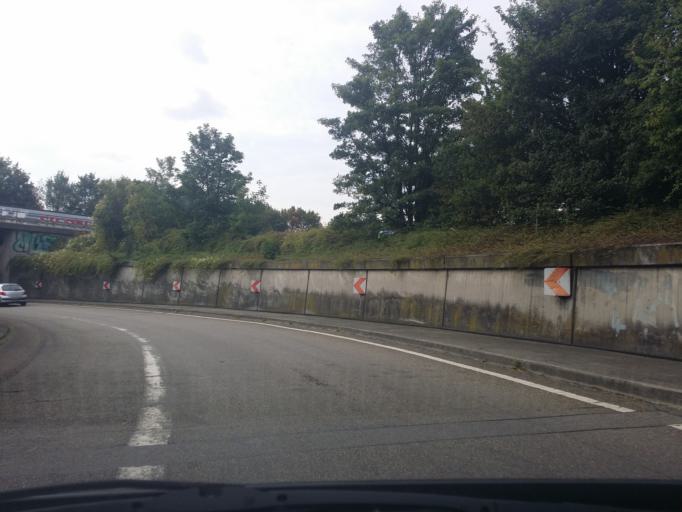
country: DE
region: Hesse
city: Sulzbach
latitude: 50.1154
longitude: 8.5306
